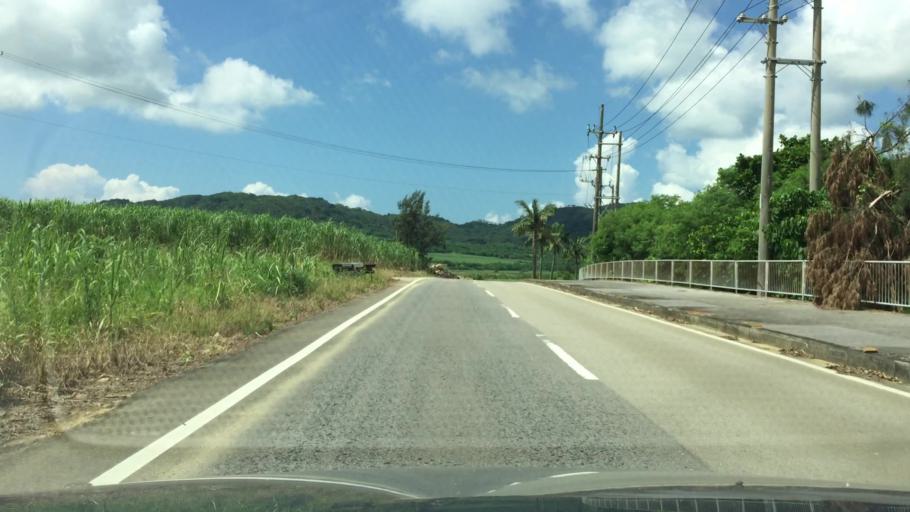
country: JP
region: Okinawa
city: Ishigaki
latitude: 24.3936
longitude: 124.1527
